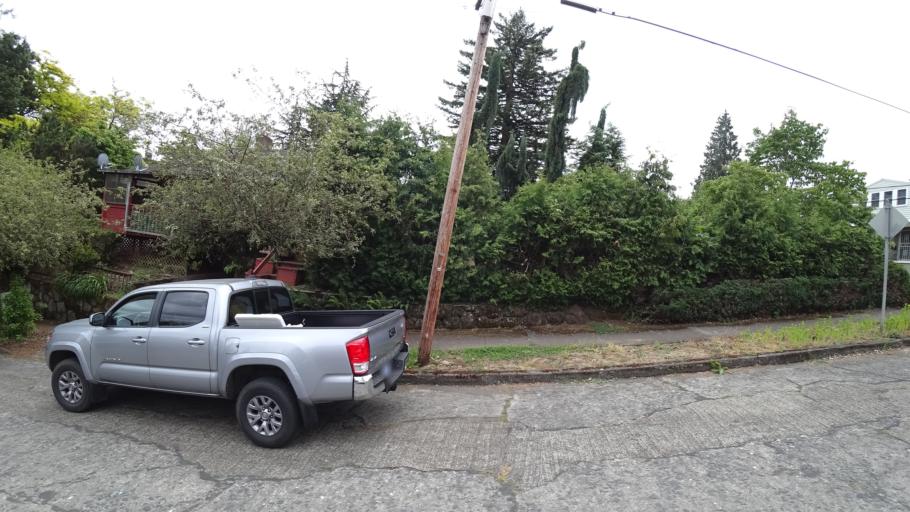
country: US
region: Oregon
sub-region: Multnomah County
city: Lents
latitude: 45.5180
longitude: -122.5875
